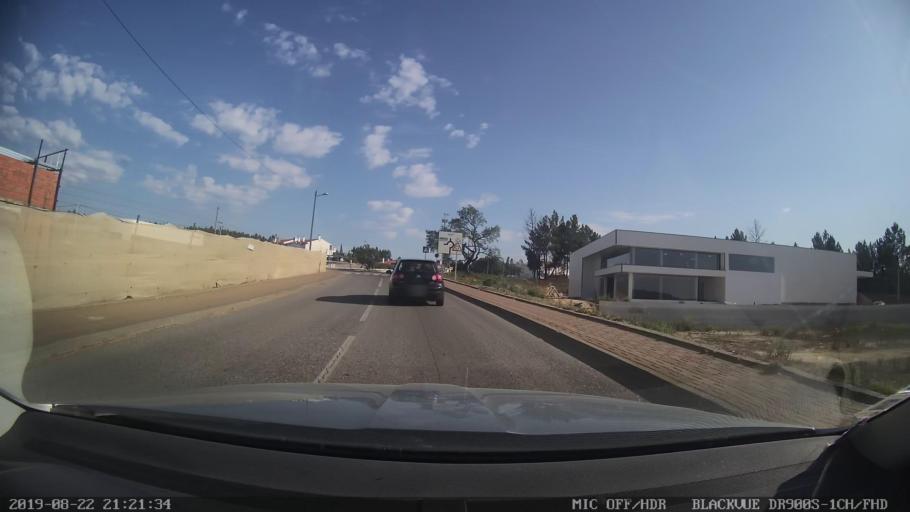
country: PT
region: Castelo Branco
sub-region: Serta
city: Serta
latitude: 39.8192
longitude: -8.1084
